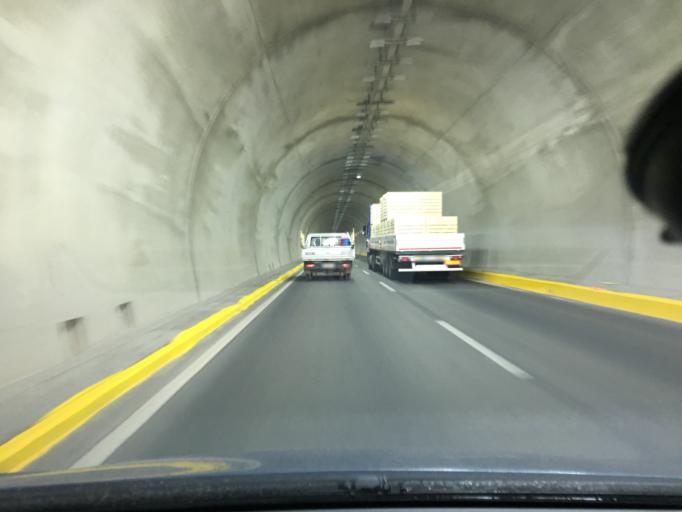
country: TR
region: Afyonkarahisar
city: Afyonkarahisar
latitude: 38.7948
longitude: 30.4362
